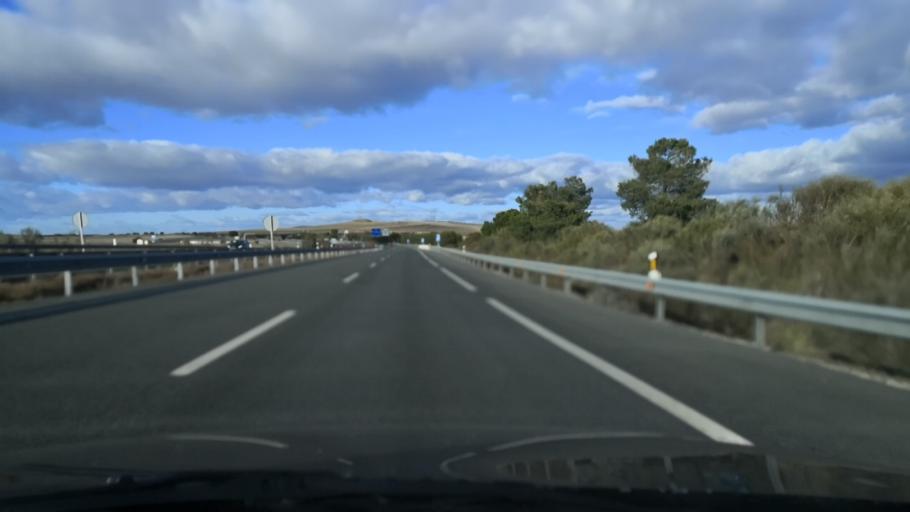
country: ES
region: Castille and Leon
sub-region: Provincia de Avila
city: Sanchidrian
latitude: 40.8951
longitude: -4.5744
